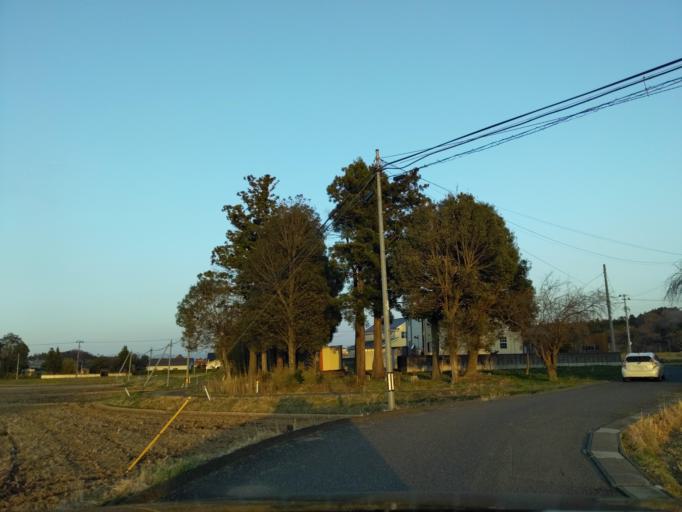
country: JP
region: Fukushima
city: Koriyama
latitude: 37.3465
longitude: 140.3036
